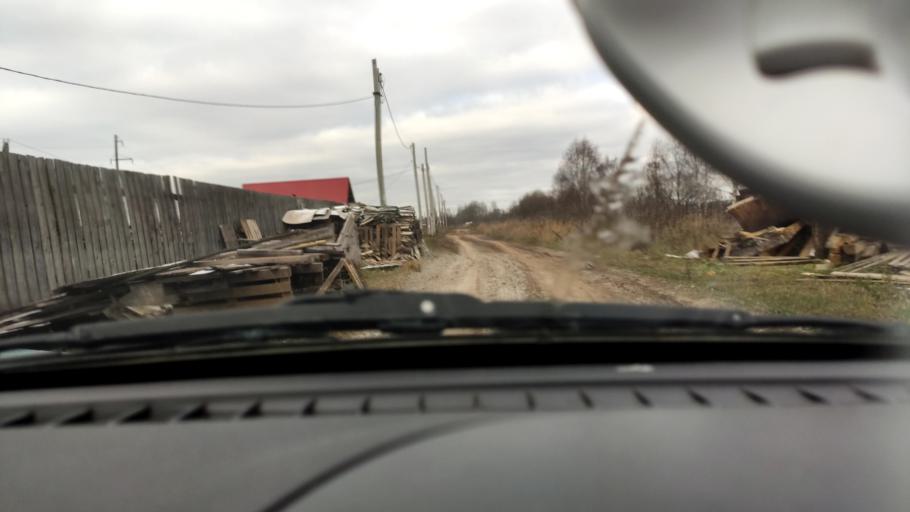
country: RU
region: Perm
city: Kondratovo
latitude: 57.9895
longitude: 56.0767
